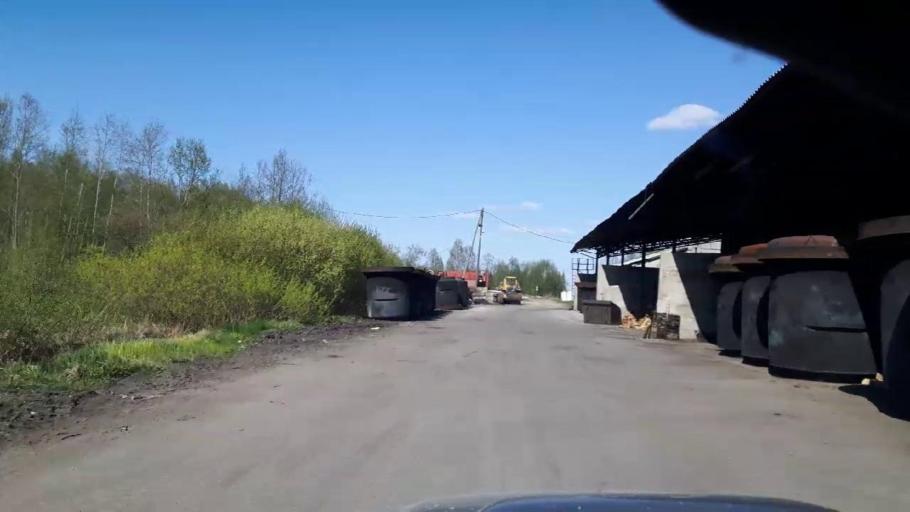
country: EE
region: Paernumaa
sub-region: Tootsi vald
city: Tootsi
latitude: 58.5221
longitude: 24.8186
